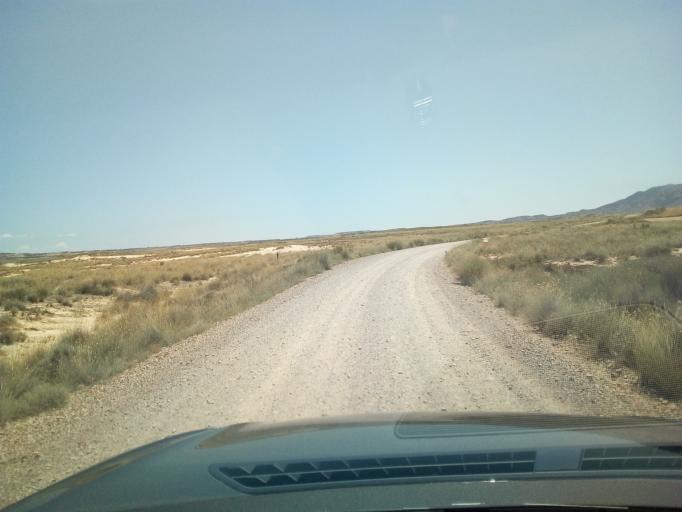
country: ES
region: Navarre
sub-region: Provincia de Navarra
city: Arguedas
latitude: 42.1817
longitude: -1.4593
